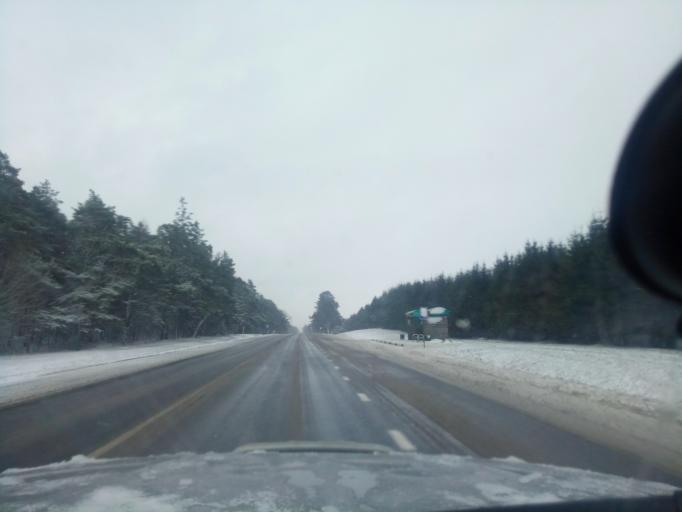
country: BY
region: Minsk
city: Haradzyeya
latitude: 53.2840
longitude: 26.5864
